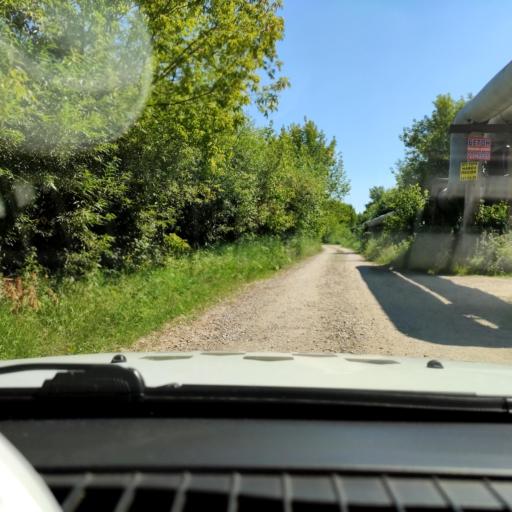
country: RU
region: Perm
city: Kondratovo
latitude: 57.9926
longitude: 56.1261
